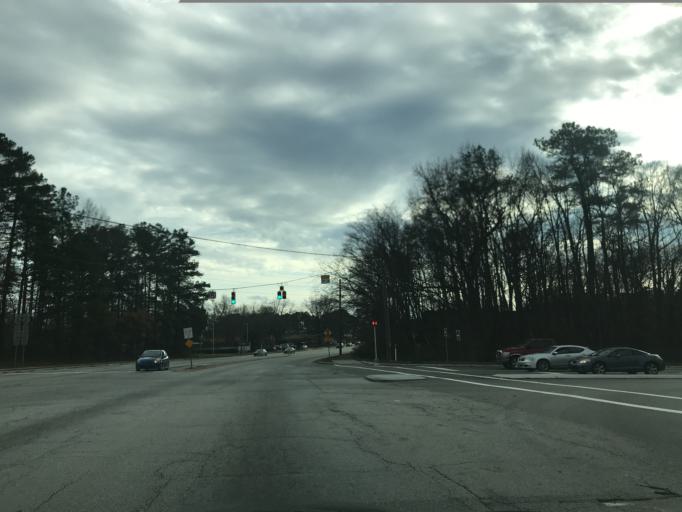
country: US
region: North Carolina
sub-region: Wake County
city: Raleigh
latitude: 35.7569
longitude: -78.6126
